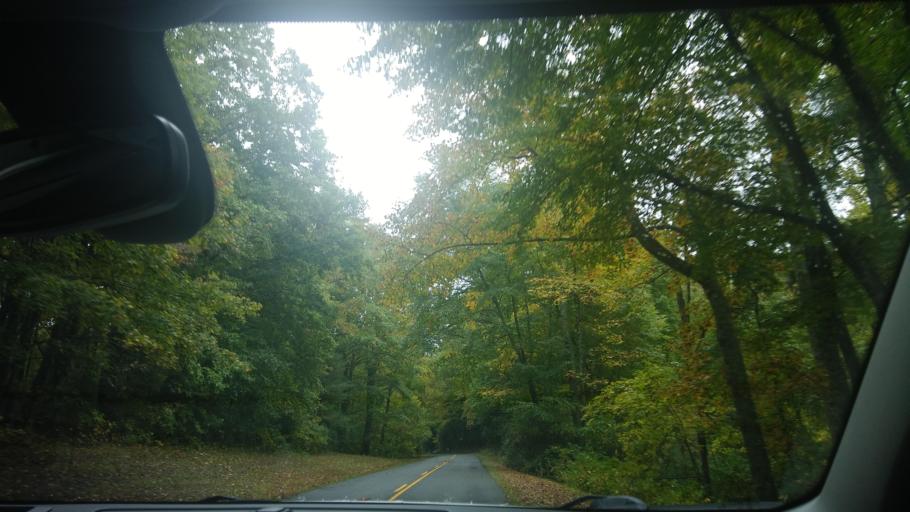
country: US
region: North Carolina
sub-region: Mitchell County
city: Spruce Pine
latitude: 35.8793
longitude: -82.0040
